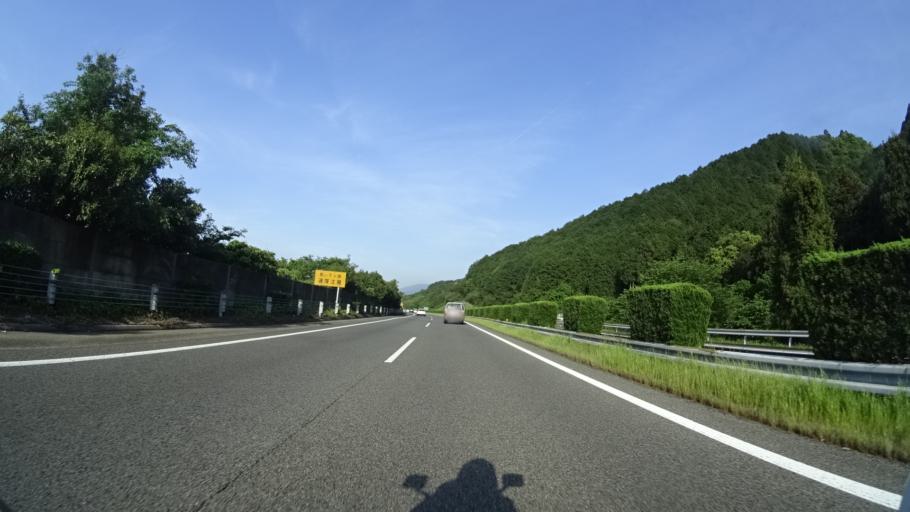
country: JP
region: Ehime
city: Niihama
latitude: 33.9526
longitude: 133.4448
